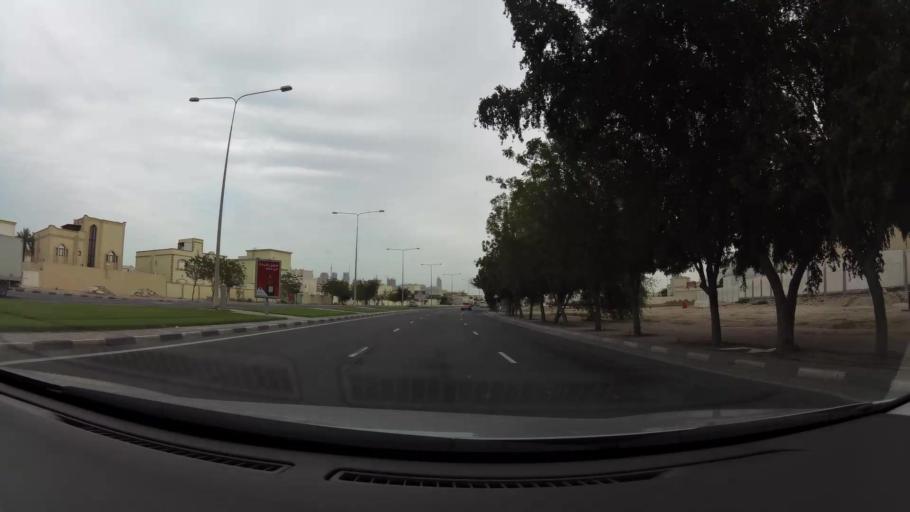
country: QA
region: Baladiyat ad Dawhah
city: Doha
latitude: 25.3458
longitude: 51.5053
